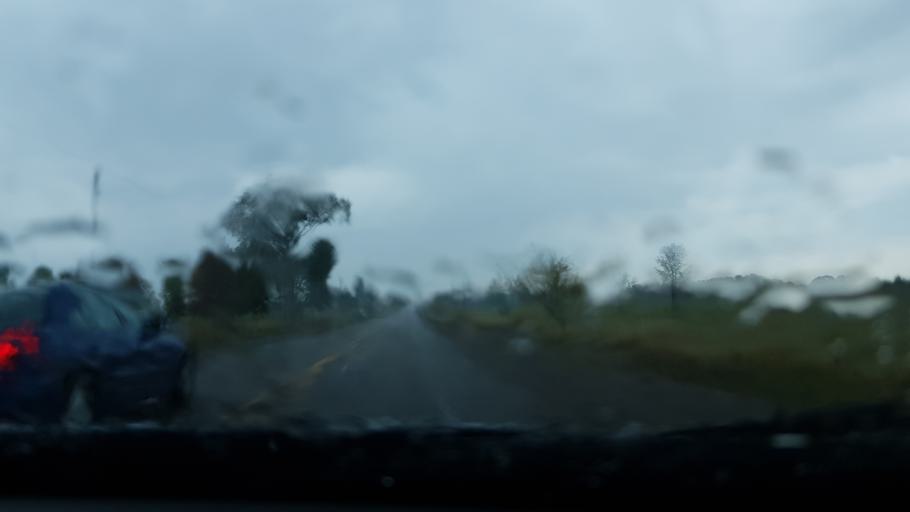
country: CA
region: Ontario
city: Omemee
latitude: 44.3859
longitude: -78.5933
